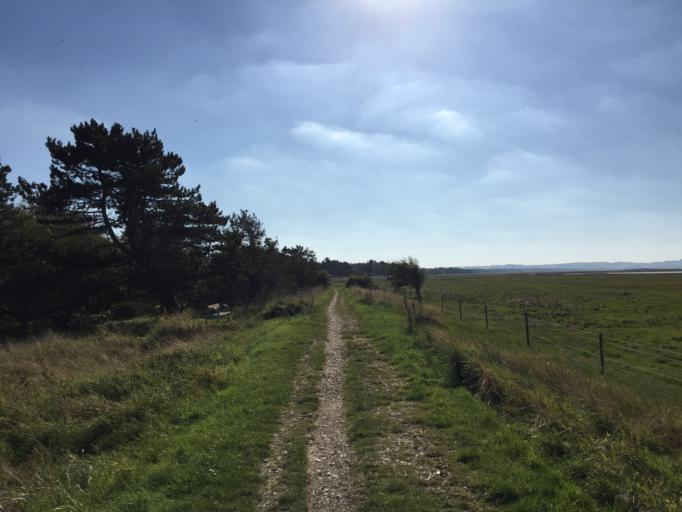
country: DK
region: Zealand
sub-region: Odsherred Kommune
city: Hojby
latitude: 55.8935
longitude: 11.5340
